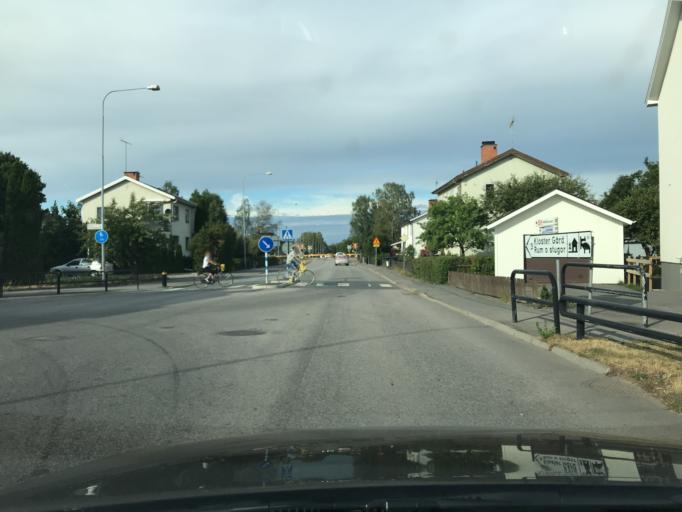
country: SE
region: Kalmar
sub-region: Hultsfreds Kommun
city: Hultsfred
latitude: 57.4919
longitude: 15.8407
